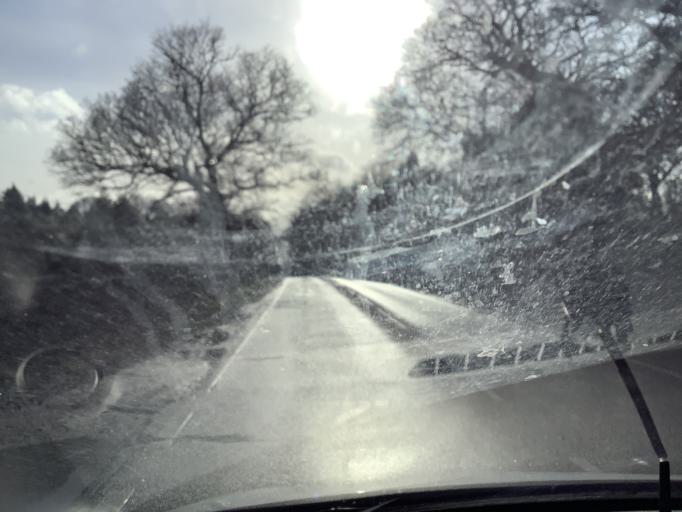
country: GB
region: England
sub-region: Hampshire
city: Hythe
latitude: 50.8242
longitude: -1.4367
